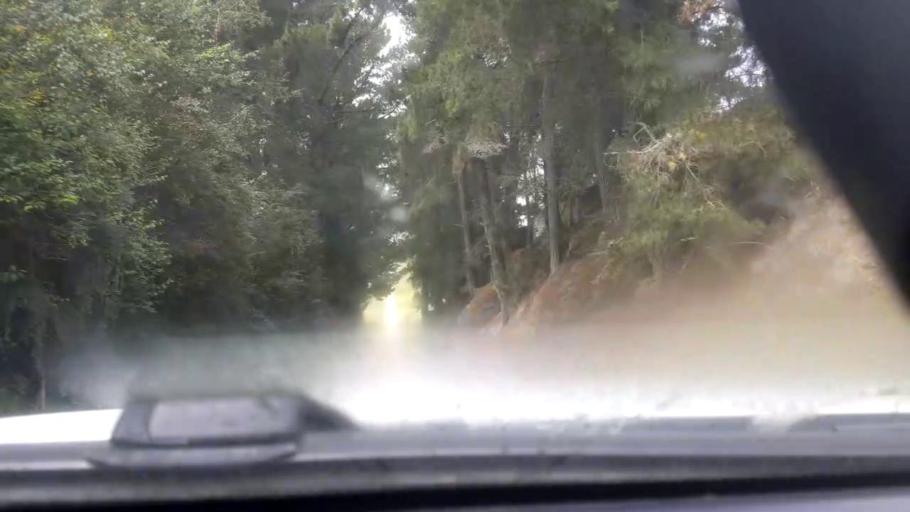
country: NZ
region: Canterbury
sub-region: Timaru District
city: Pleasant Point
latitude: -44.1954
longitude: 171.0915
